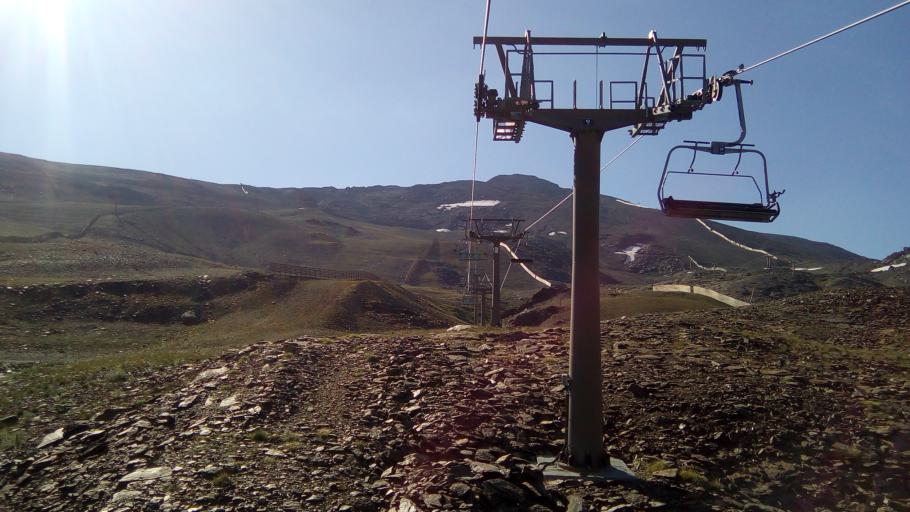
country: ES
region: Andalusia
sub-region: Provincia de Granada
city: Guejar-Sierra
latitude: 37.0675
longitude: -3.3817
